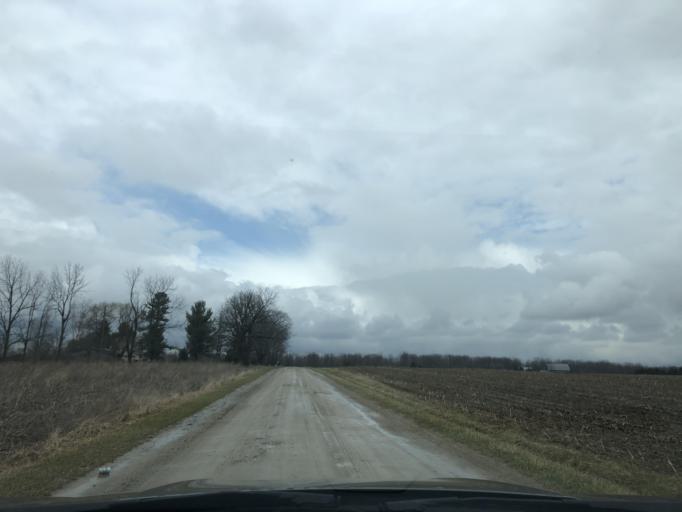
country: US
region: Michigan
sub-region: Clinton County
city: Saint Johns
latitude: 43.0408
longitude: -84.6411
